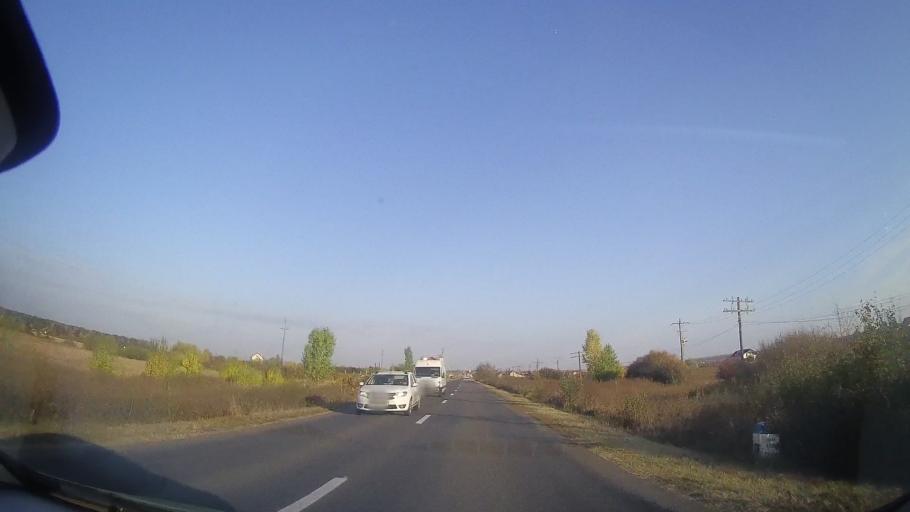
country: RO
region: Timis
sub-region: Comuna Pischia
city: Pischia
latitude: 45.8929
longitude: 21.3464
